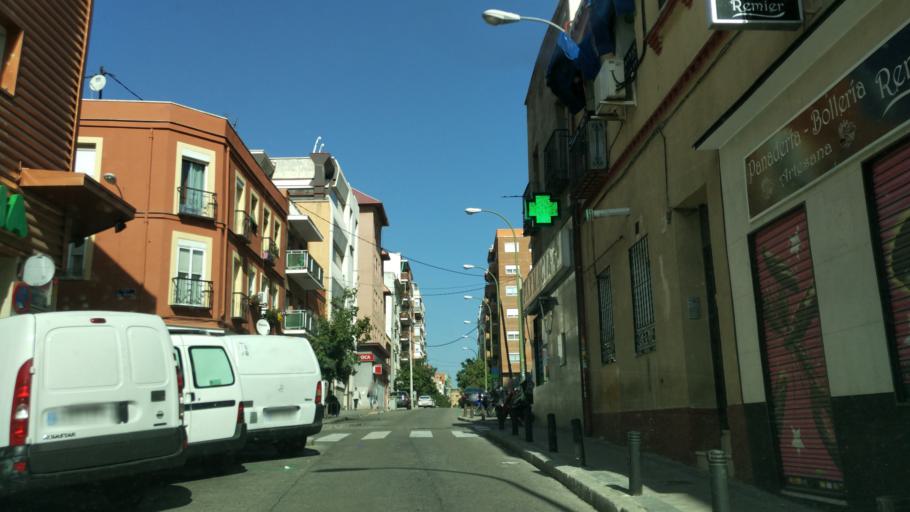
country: ES
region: Madrid
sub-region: Provincia de Madrid
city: Tetuan de las Victorias
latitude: 40.4558
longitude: -3.7002
